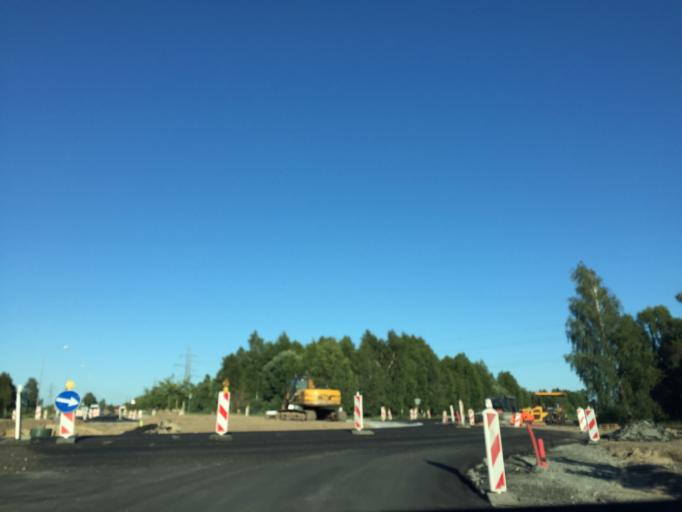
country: LV
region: Ventspils
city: Ventspils
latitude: 57.3976
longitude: 21.6316
